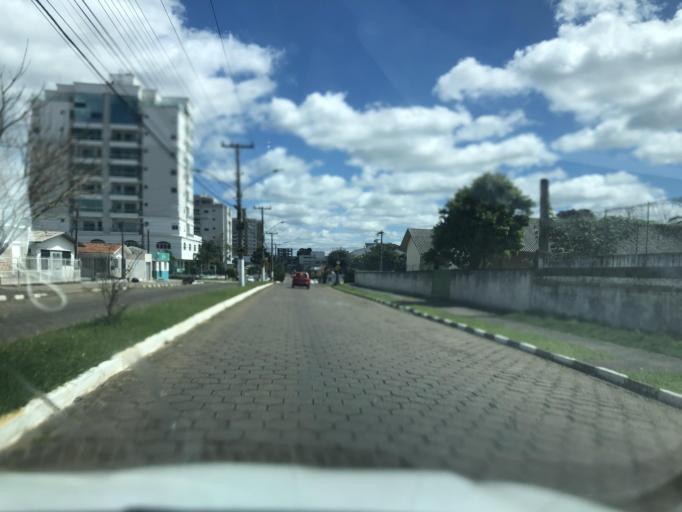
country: BR
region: Santa Catarina
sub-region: Lages
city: Lages
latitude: -27.8170
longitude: -50.3138
